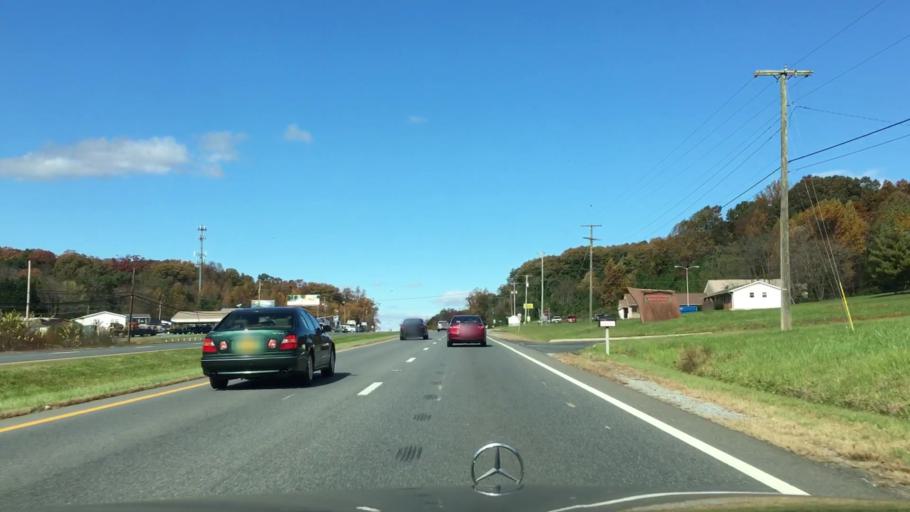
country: US
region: Virginia
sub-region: Campbell County
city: Rustburg
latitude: 37.2951
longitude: -79.1710
